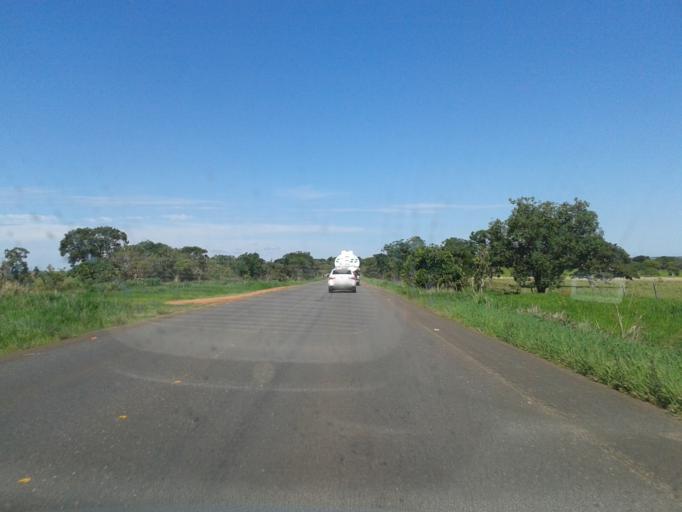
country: BR
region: Goias
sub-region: Bela Vista De Goias
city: Bela Vista de Goias
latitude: -17.0916
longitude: -48.8693
